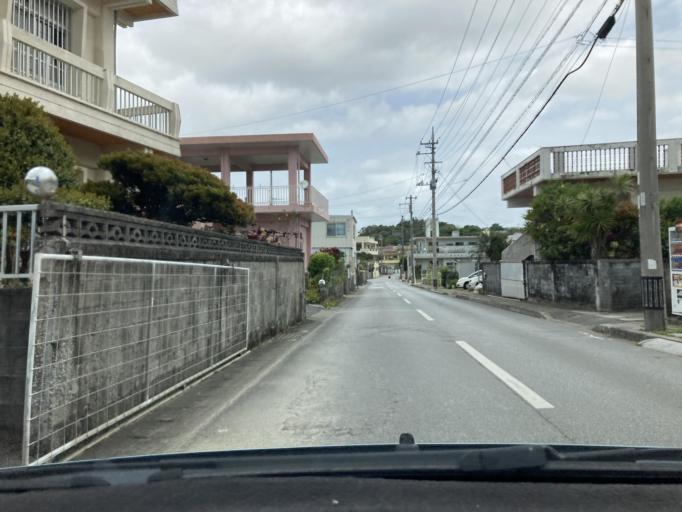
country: JP
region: Okinawa
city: Ginowan
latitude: 26.2314
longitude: 127.7437
